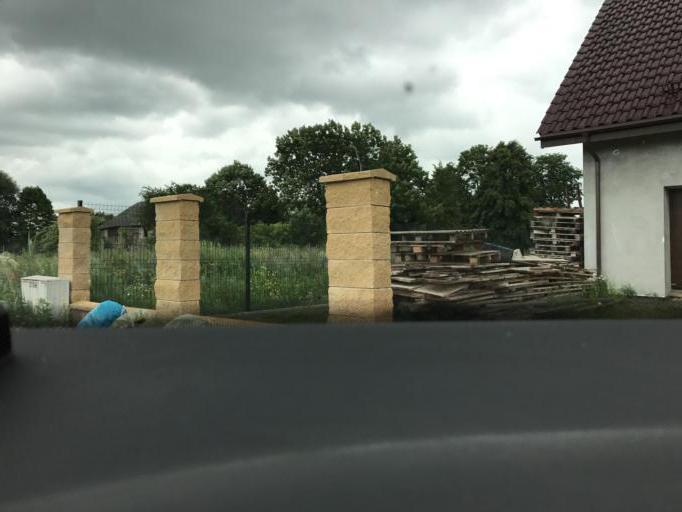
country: PL
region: Pomeranian Voivodeship
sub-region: Powiat gdanski
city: Pruszcz Gdanski
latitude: 54.2816
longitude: 18.6497
